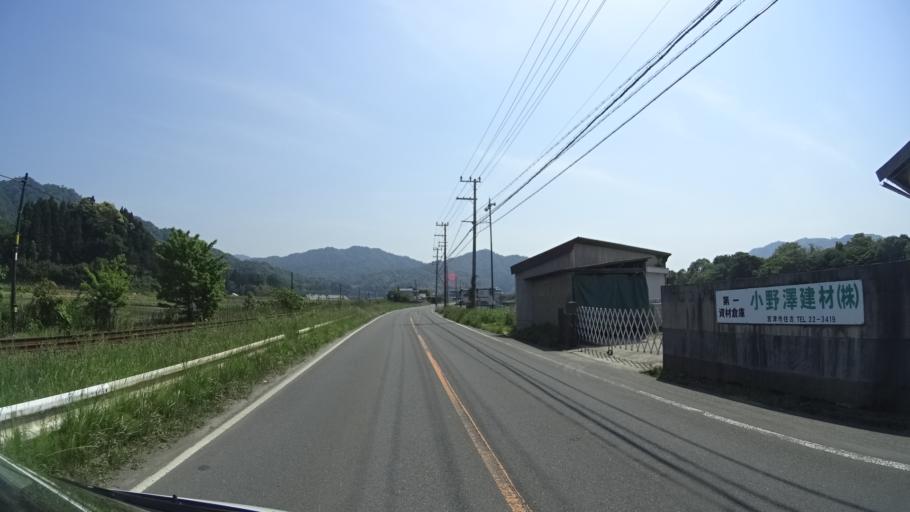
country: JP
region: Kyoto
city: Miyazu
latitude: 35.5564
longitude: 135.1637
